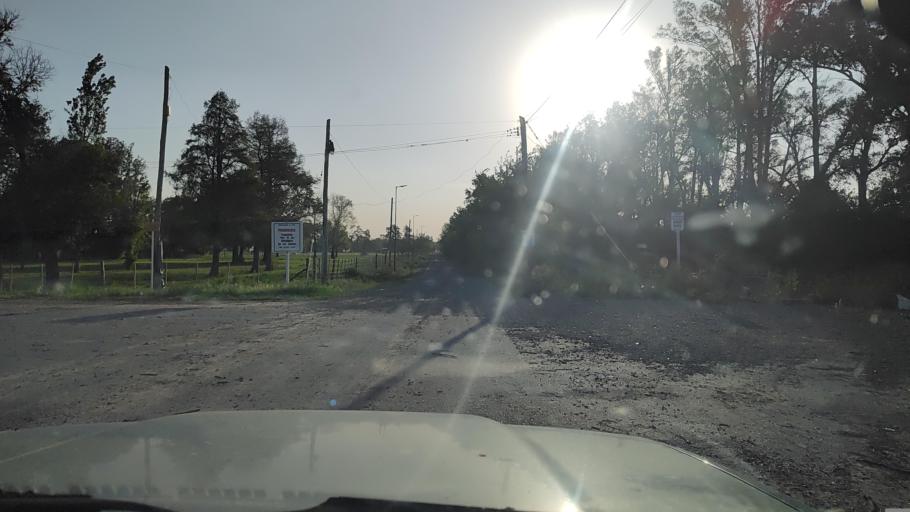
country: AR
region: Buenos Aires
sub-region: Partido de Lujan
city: Lujan
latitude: -34.5508
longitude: -59.1969
